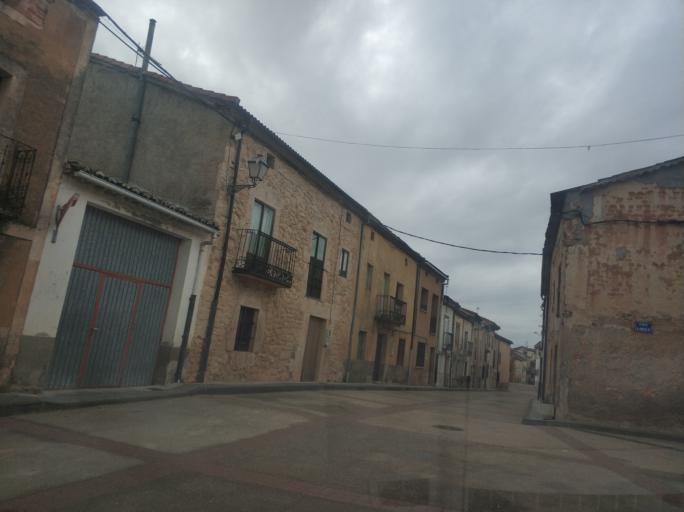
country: ES
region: Castille and Leon
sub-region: Provincia de Soria
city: Alcubilla de Avellaneda
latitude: 41.7256
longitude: -3.3041
